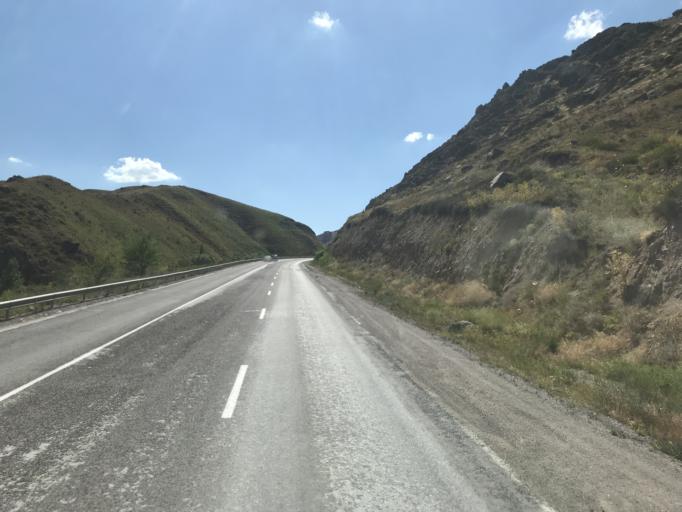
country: KZ
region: Zhambyl
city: Georgiyevka
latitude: 43.3576
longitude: 75.0174
